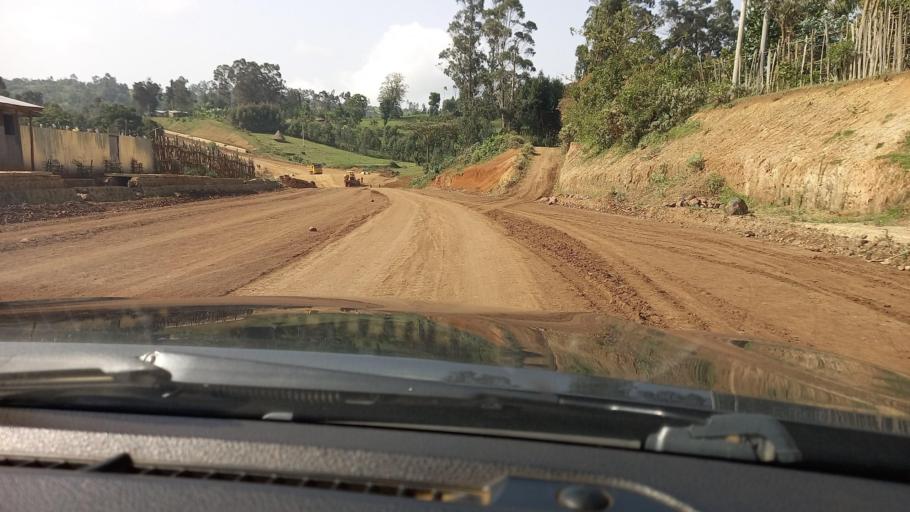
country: ET
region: Southern Nations, Nationalities, and People's Region
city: Mizan Teferi
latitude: 6.1697
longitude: 35.5848
